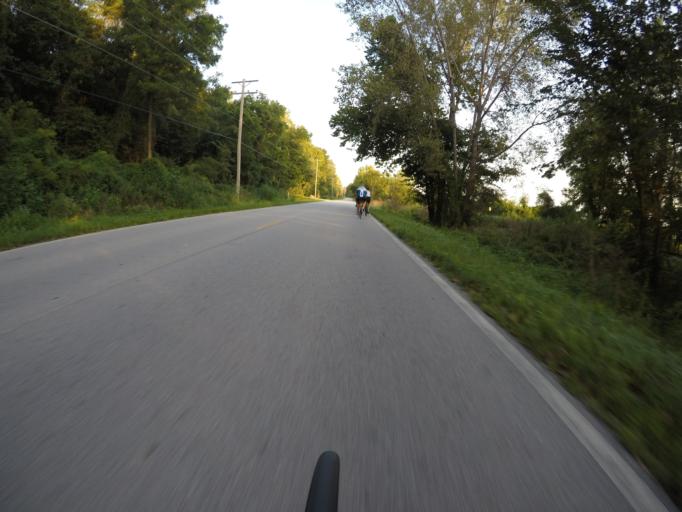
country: US
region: Kansas
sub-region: Leavenworth County
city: Lansing
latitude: 39.1964
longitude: -94.8116
